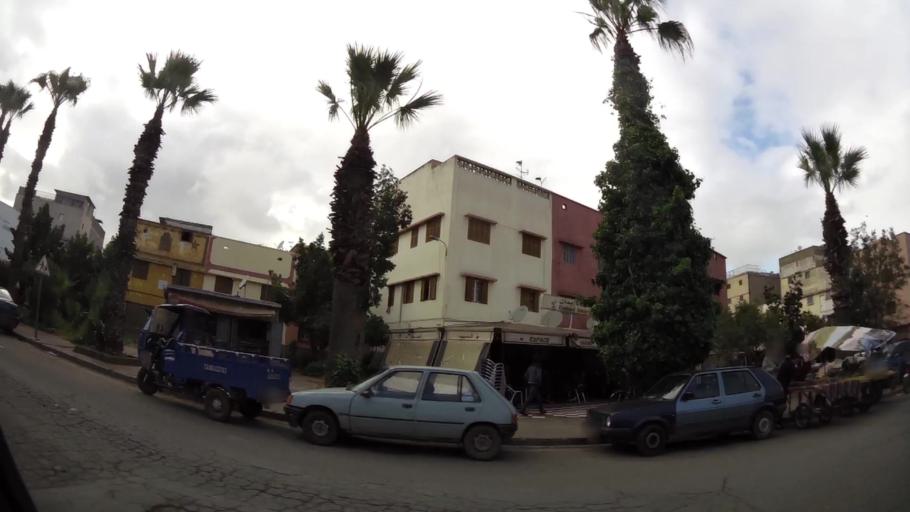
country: MA
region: Grand Casablanca
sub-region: Mohammedia
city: Mohammedia
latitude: 33.6818
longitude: -7.3879
